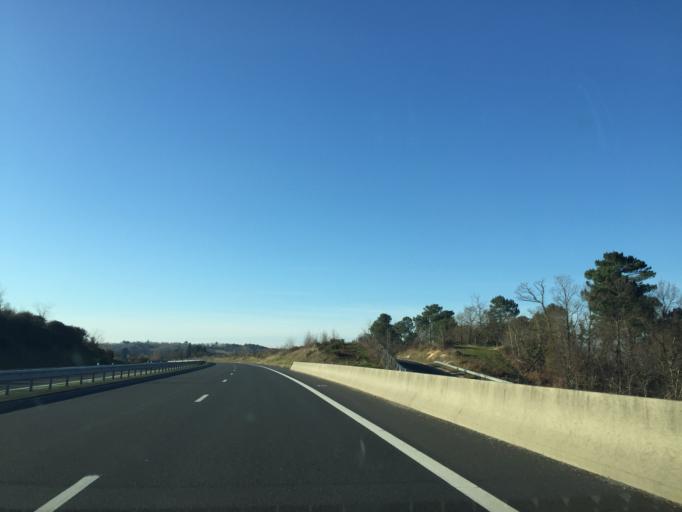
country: FR
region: Limousin
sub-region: Departement de la Correze
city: Cublac
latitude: 45.1735
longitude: 1.3149
